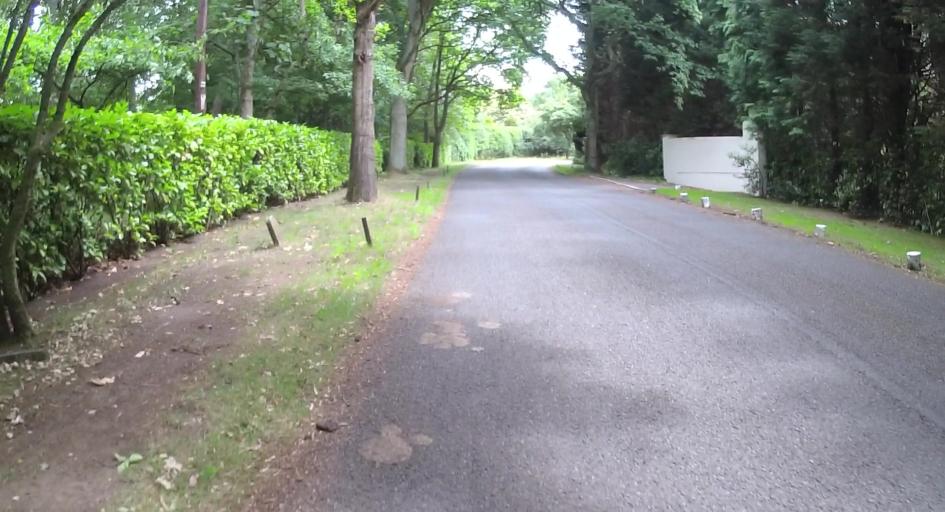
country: GB
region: England
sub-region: Surrey
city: Hale
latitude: 51.2121
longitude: -0.7644
